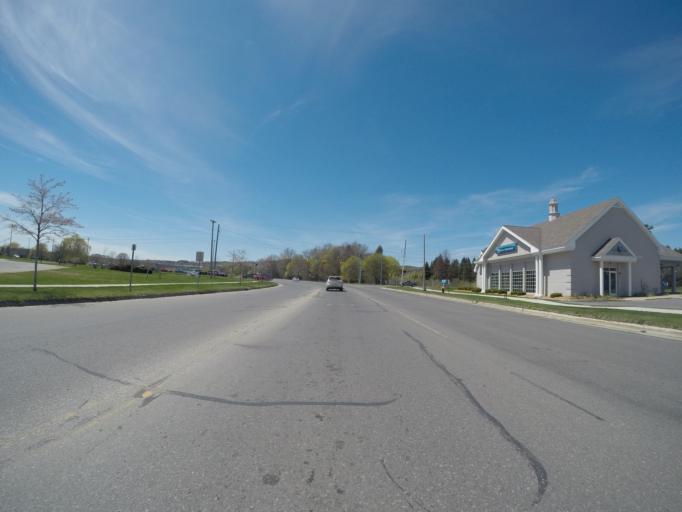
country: US
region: Michigan
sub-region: Grand Traverse County
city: Traverse City
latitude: 44.7517
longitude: -85.6340
